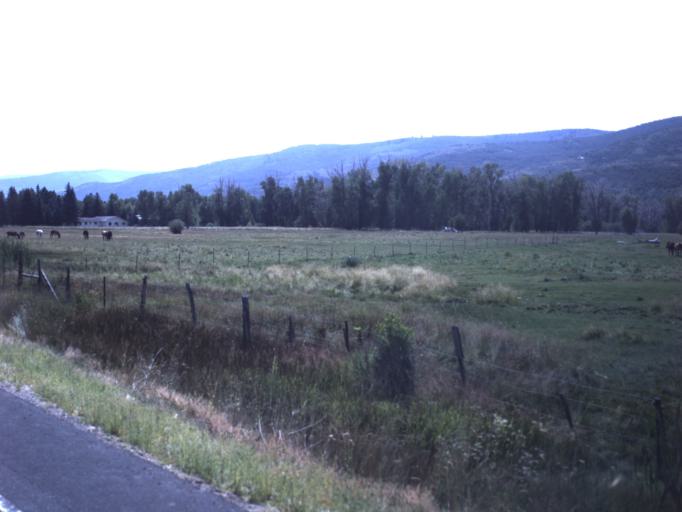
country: US
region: Utah
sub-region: Summit County
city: Francis
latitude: 40.5834
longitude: -111.2363
